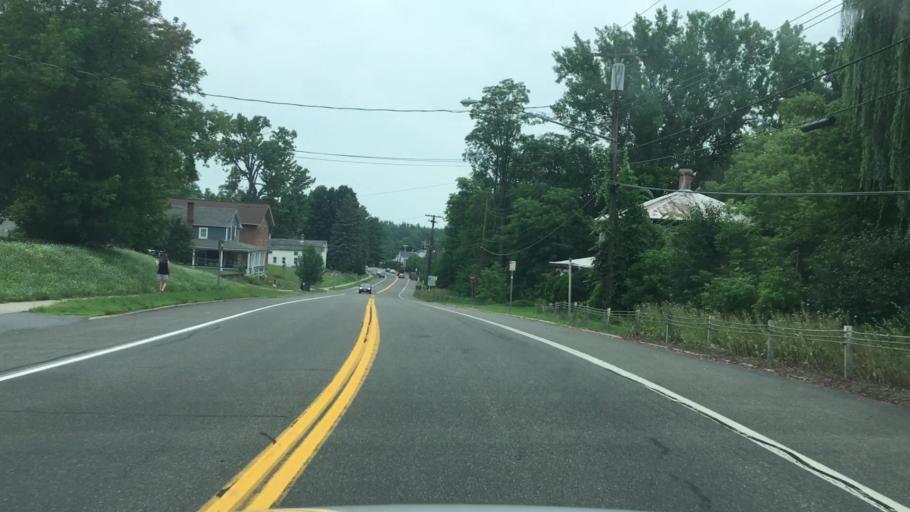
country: US
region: New York
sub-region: Essex County
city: Keeseville
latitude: 44.5029
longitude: -73.4854
